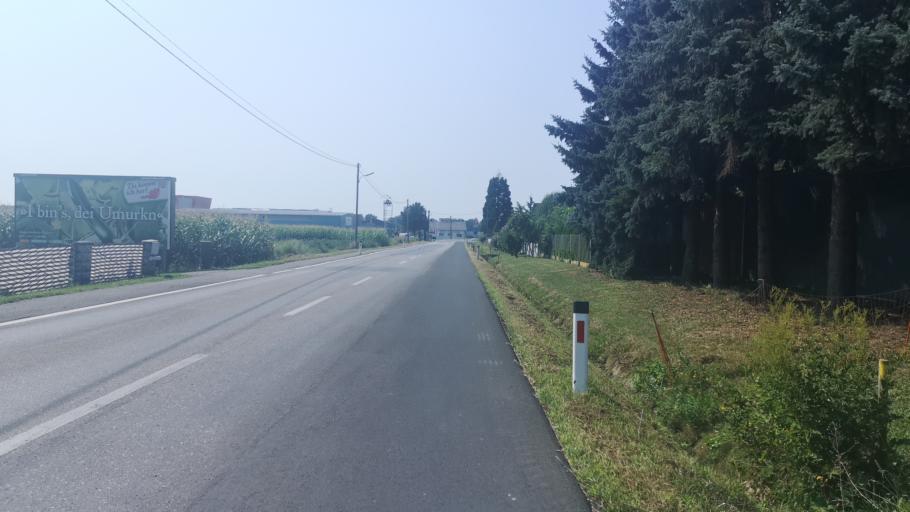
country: AT
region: Styria
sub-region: Politischer Bezirk Graz-Umgebung
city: Seiersberg
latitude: 46.9989
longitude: 15.4003
